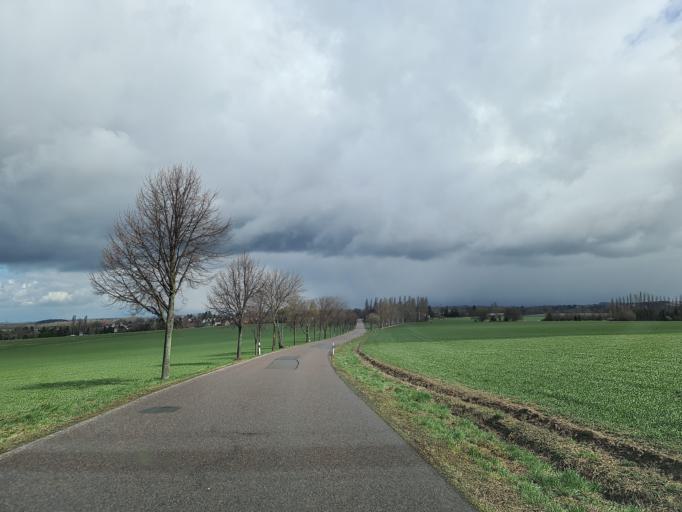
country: DE
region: Saxony
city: Limbach-Oberfrohna
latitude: 50.8396
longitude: 12.7287
